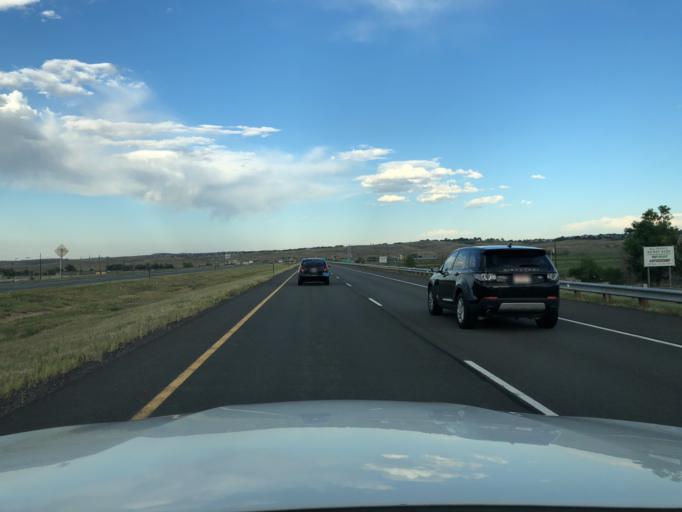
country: US
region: Colorado
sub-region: Boulder County
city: Louisville
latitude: 39.9581
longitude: -105.1009
